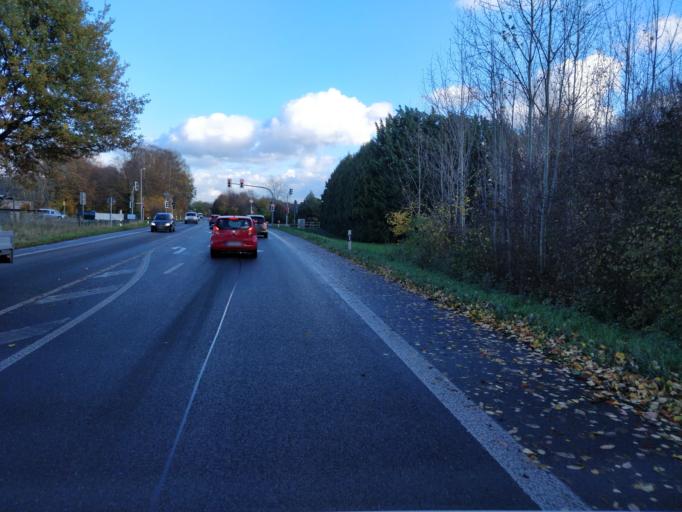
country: DE
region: North Rhine-Westphalia
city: Rees
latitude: 51.7667
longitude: 6.3987
